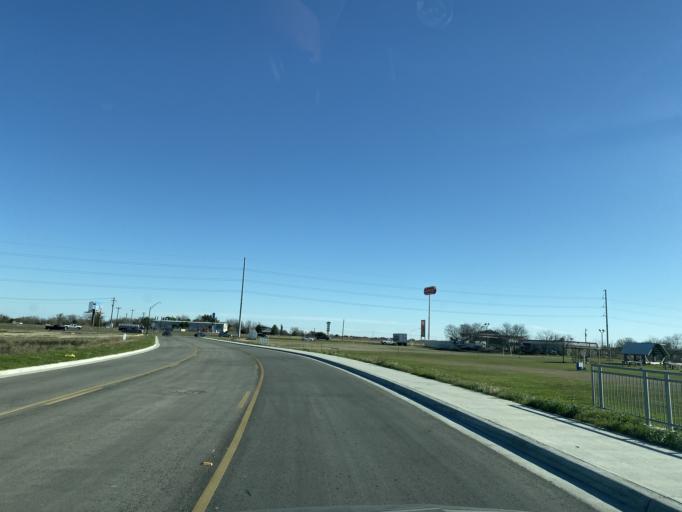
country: US
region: Texas
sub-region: Hays County
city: Kyle
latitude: 30.0001
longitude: -97.8708
